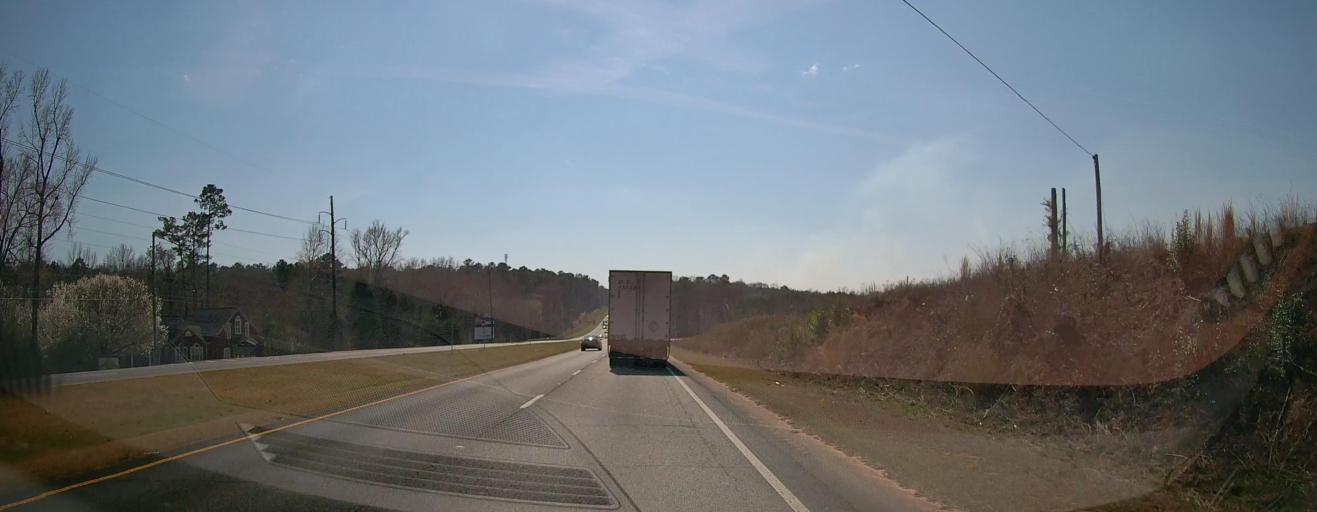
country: US
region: Georgia
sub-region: Jones County
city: Gray
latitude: 32.9900
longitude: -83.5670
